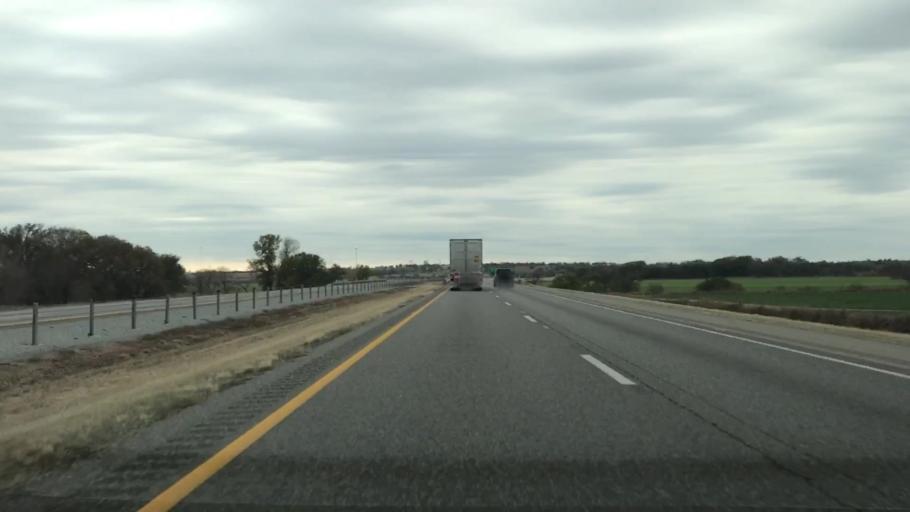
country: US
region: Oklahoma
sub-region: Custer County
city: Clinton
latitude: 35.5046
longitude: -98.9389
